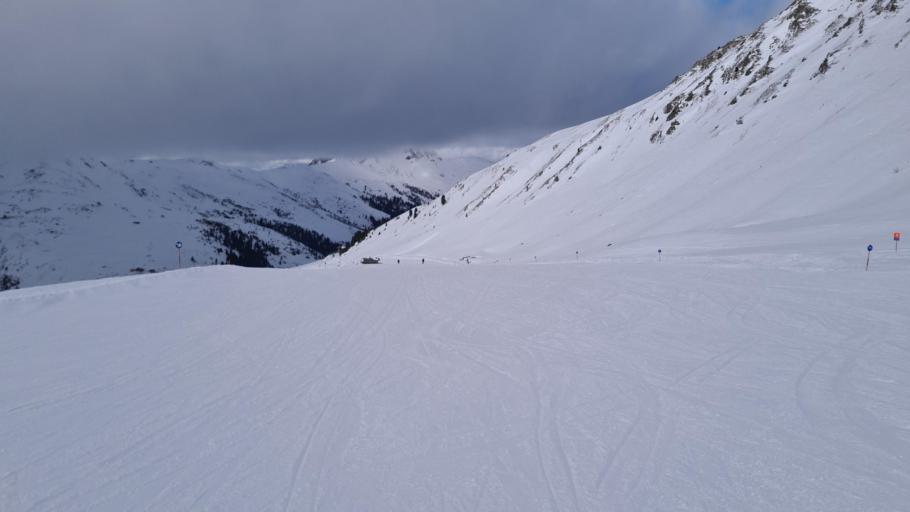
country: AT
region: Salzburg
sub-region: Politischer Bezirk Zell am See
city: Neukirchen am Grossvenediger
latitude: 47.2874
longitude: 12.2926
